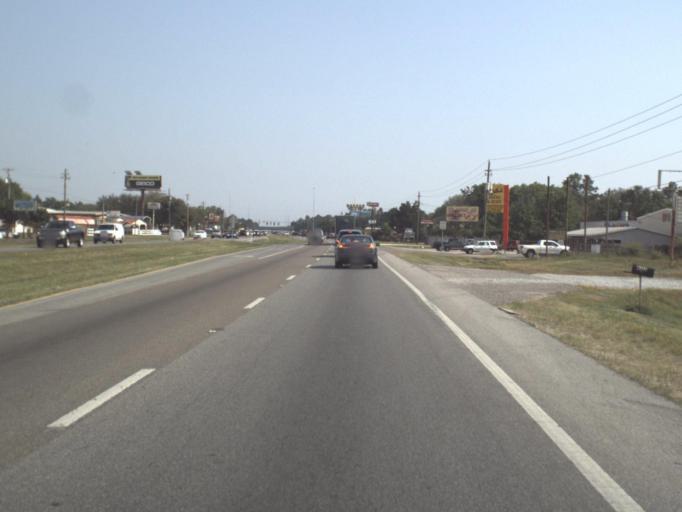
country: US
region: Florida
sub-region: Escambia County
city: Ensley
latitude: 30.5152
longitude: -87.2719
